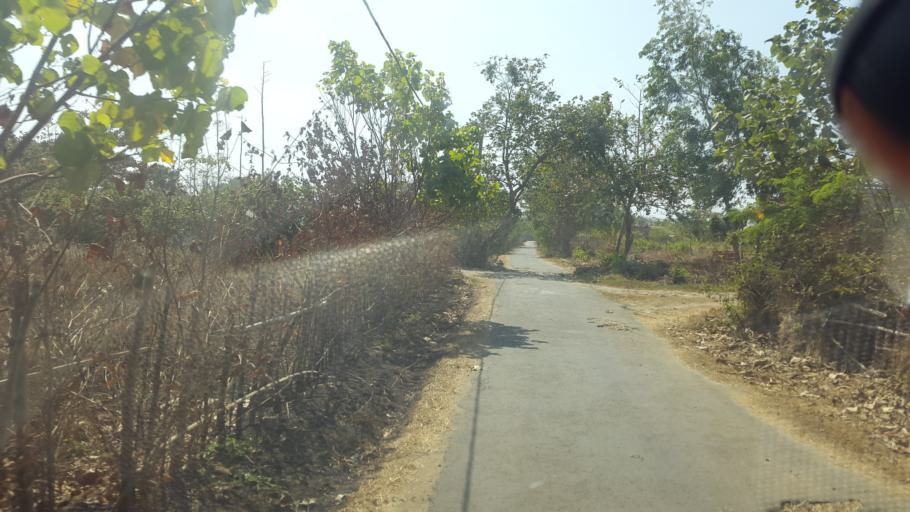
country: ID
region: West Java
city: Gunungbatu
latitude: -7.3358
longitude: 106.4002
